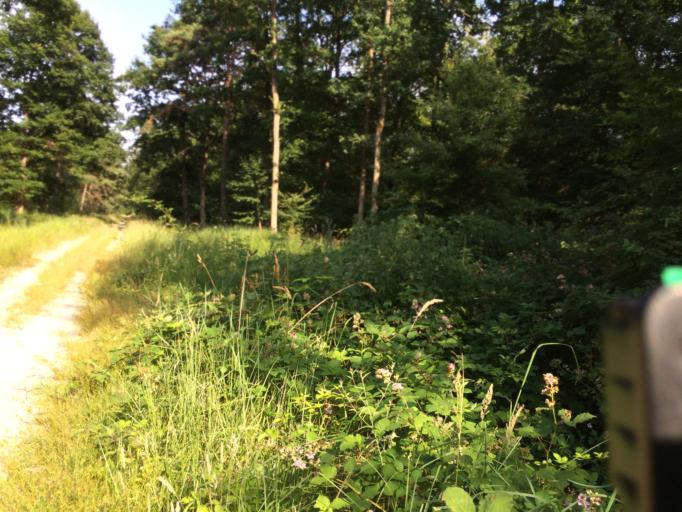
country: FR
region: Ile-de-France
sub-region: Departement de l'Essonne
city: Soisy-sur-Seine
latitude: 48.6677
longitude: 2.4738
